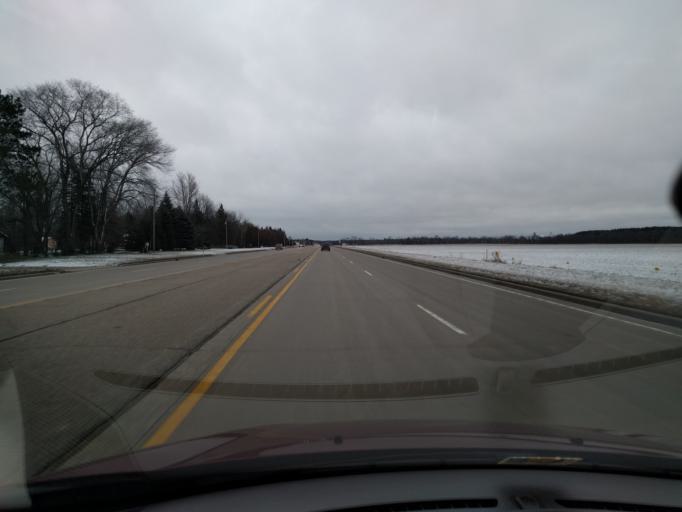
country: US
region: Wisconsin
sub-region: Portage County
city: Whiting
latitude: 44.5235
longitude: -89.4881
